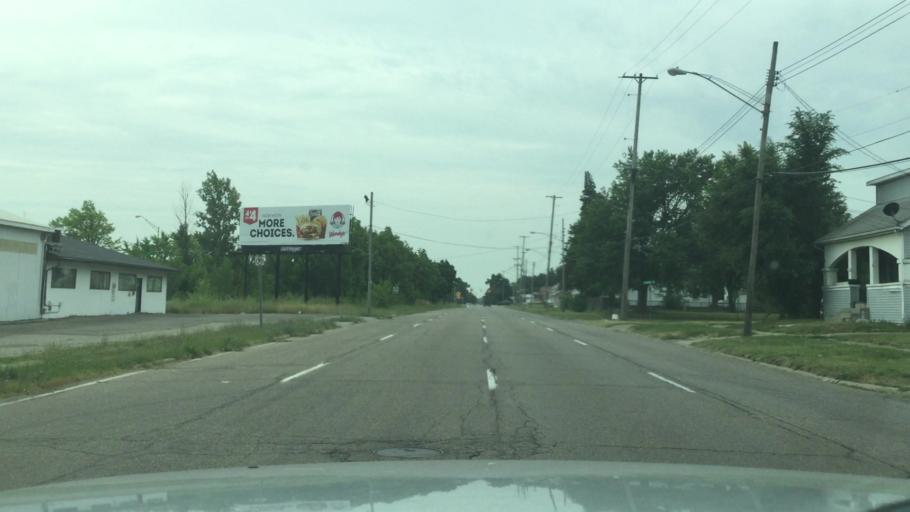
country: US
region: Michigan
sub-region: Genesee County
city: Flint
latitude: 42.9923
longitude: -83.6834
